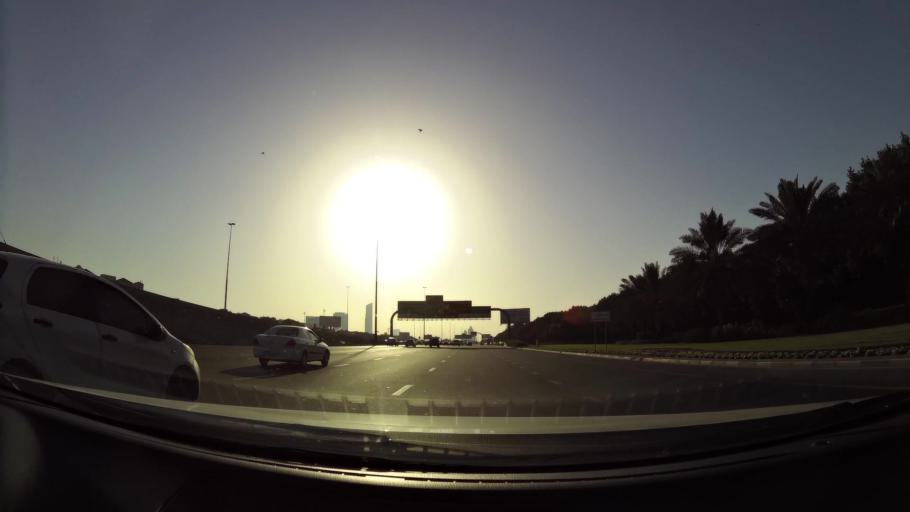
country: AE
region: Ash Shariqah
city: Sharjah
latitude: 25.2202
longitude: 55.3720
